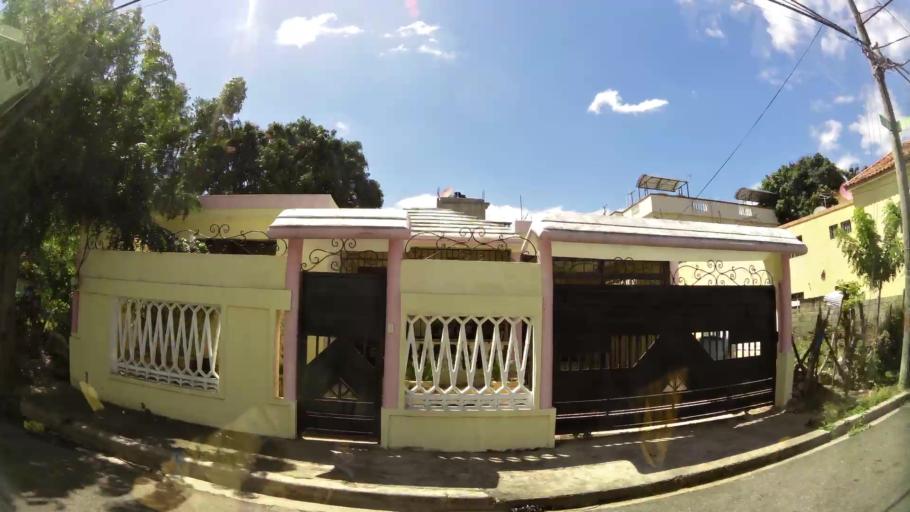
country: DO
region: San Cristobal
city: San Cristobal
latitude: 18.4138
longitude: -70.0905
